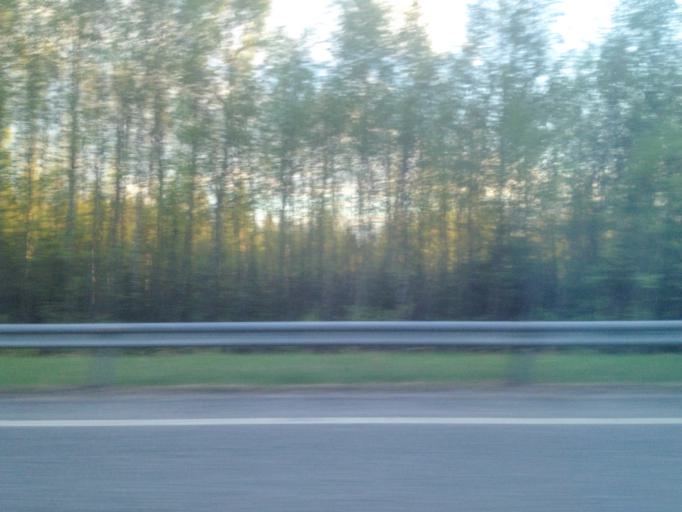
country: FI
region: Haeme
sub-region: Haemeenlinna
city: Tervakoski
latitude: 60.8193
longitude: 24.6707
